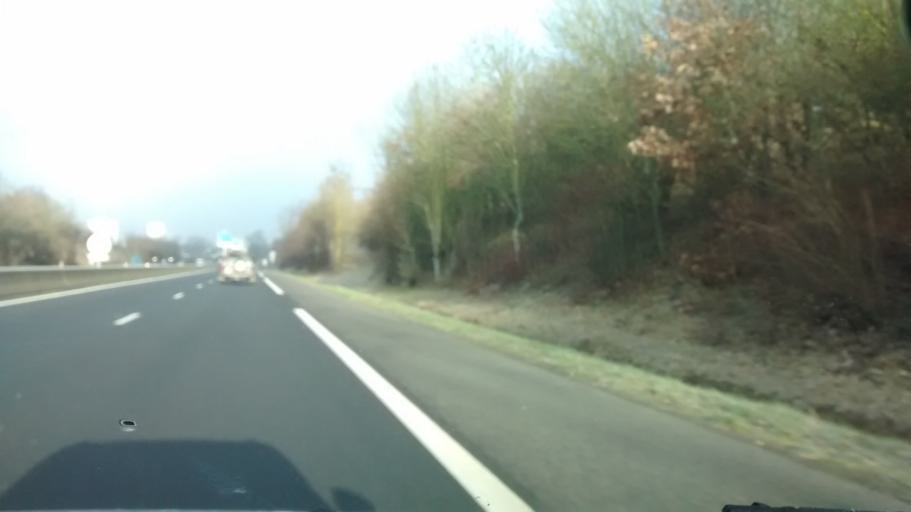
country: FR
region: Centre
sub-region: Departement d'Indre-et-Loire
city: Joue-les-Tours
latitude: 47.3356
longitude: 0.6709
